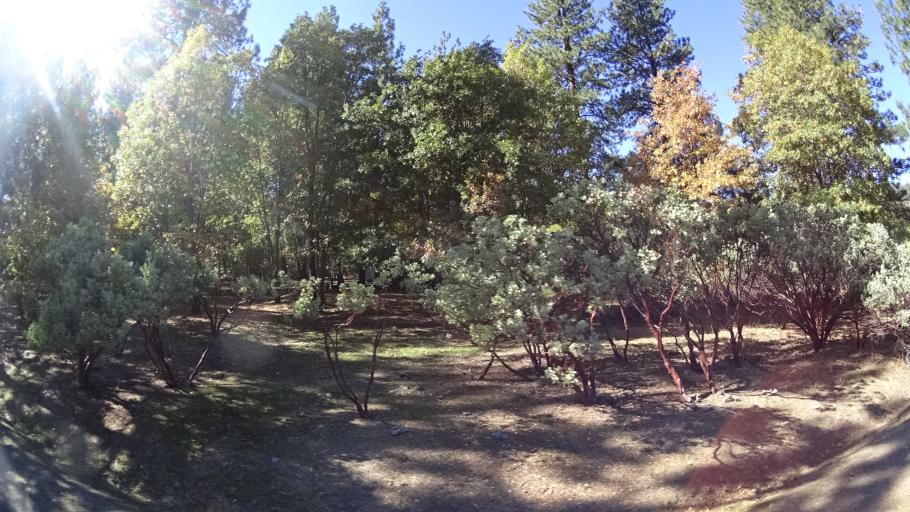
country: US
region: California
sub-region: Siskiyou County
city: Yreka
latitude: 41.5216
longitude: -122.9216
